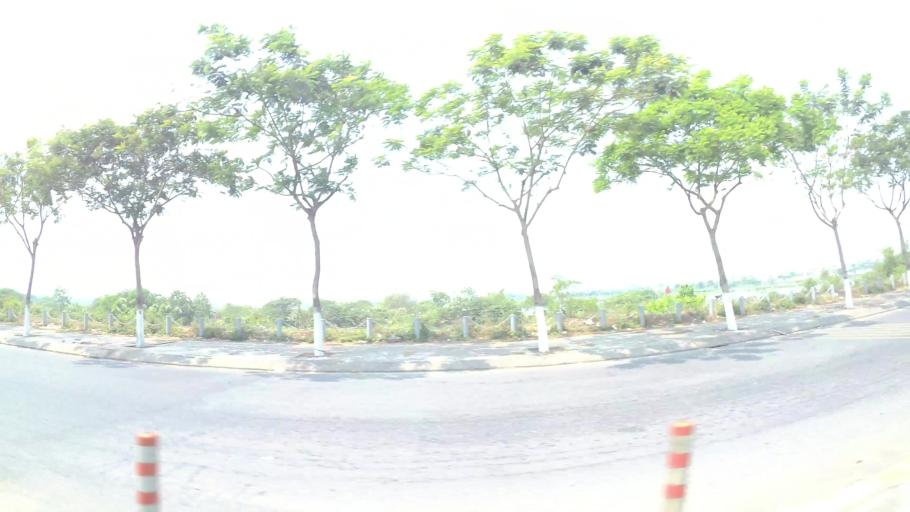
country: VN
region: Da Nang
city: Cam Le
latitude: 16.0064
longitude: 108.2079
